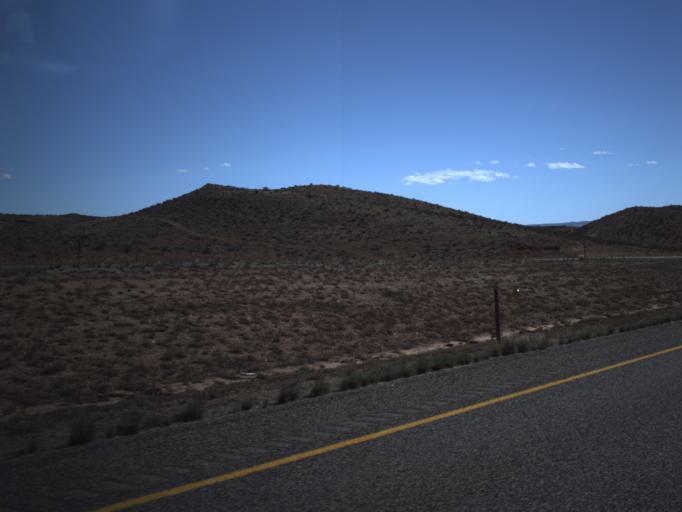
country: US
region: Utah
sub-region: Washington County
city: Saint George
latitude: 37.0169
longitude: -113.5960
